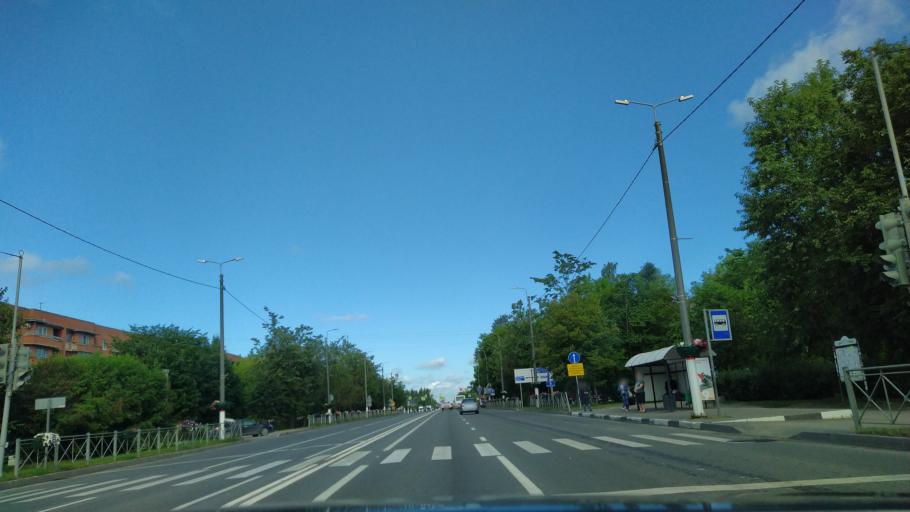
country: RU
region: Leningrad
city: Tosno
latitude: 59.5434
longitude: 30.8727
